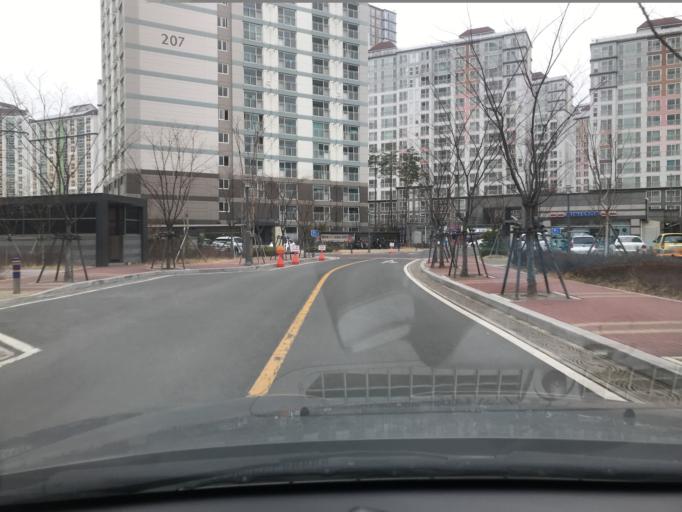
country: KR
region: Daegu
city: Hwawon
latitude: 35.6906
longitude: 128.4518
